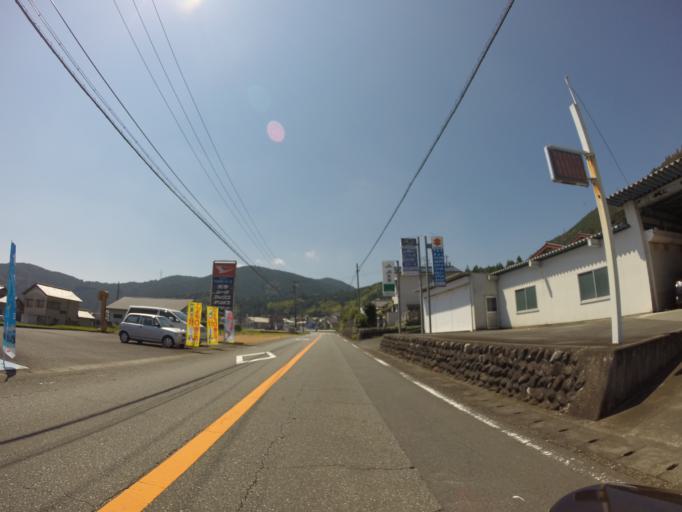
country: JP
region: Shizuoka
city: Fujinomiya
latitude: 35.1897
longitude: 138.5841
